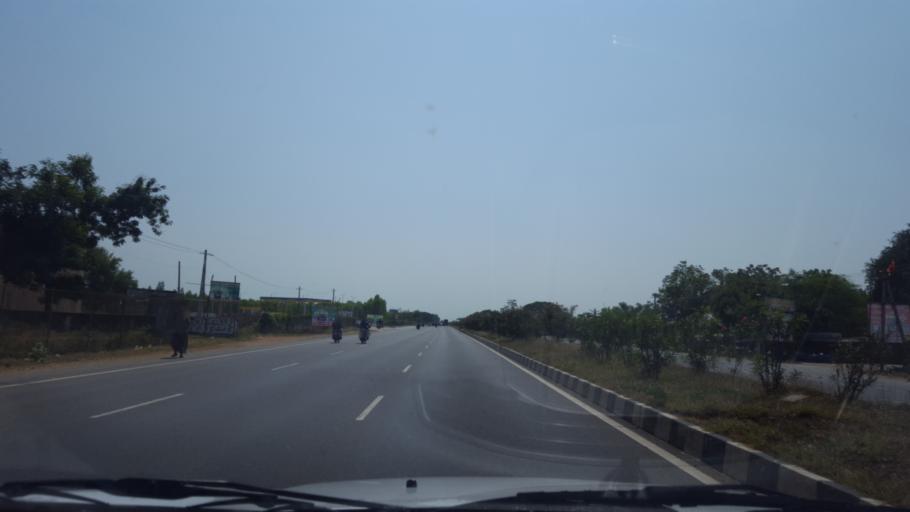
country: IN
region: Andhra Pradesh
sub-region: Prakasam
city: Ongole
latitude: 15.5977
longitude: 80.0318
